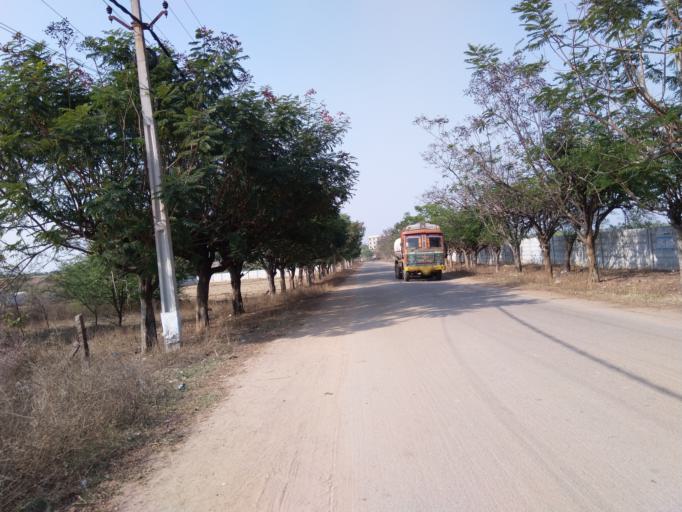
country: IN
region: Telangana
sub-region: Rangareddi
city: Quthbullapur
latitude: 17.5940
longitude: 78.4176
